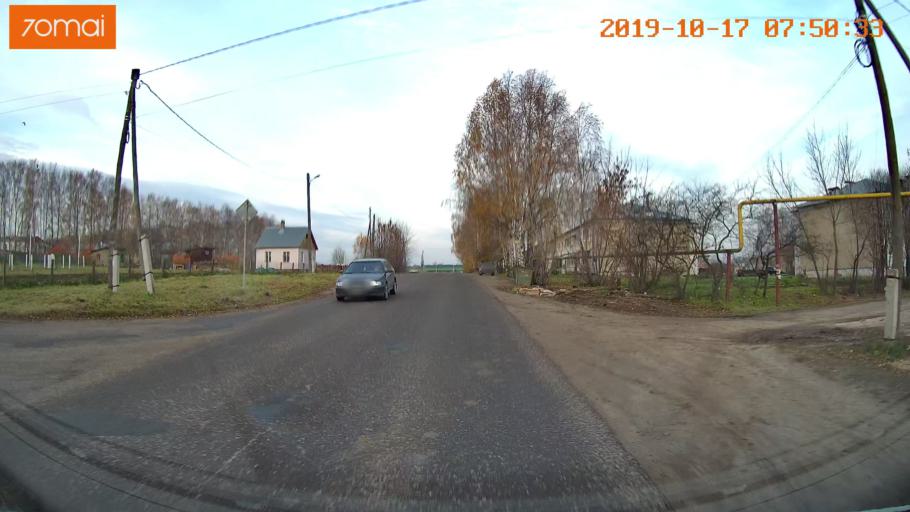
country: RU
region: Vladimir
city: Yur'yev-Pol'skiy
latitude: 56.4841
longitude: 39.6641
